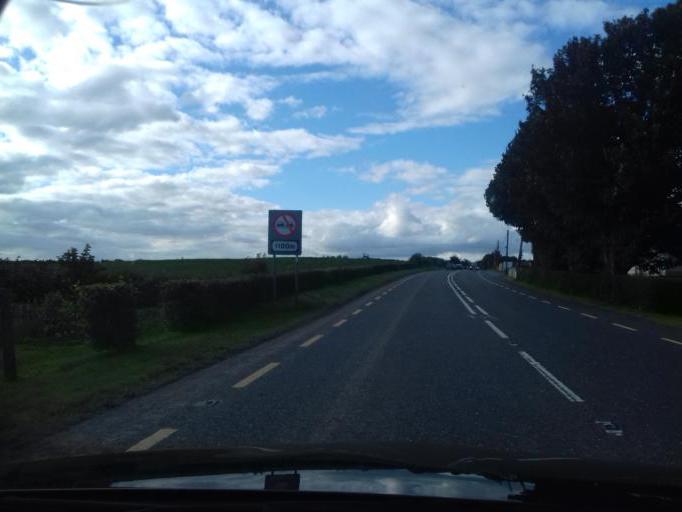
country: IE
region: Leinster
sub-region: Uibh Fhaili
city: Tullamore
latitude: 53.3111
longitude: -7.5019
